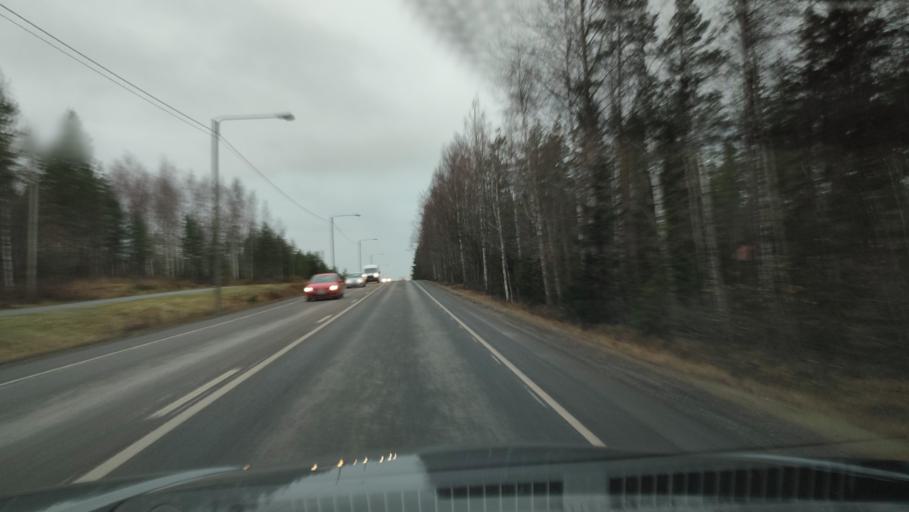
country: FI
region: Southern Ostrobothnia
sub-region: Seinaejoki
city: Seinaejoki
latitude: 62.7822
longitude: 22.7069
